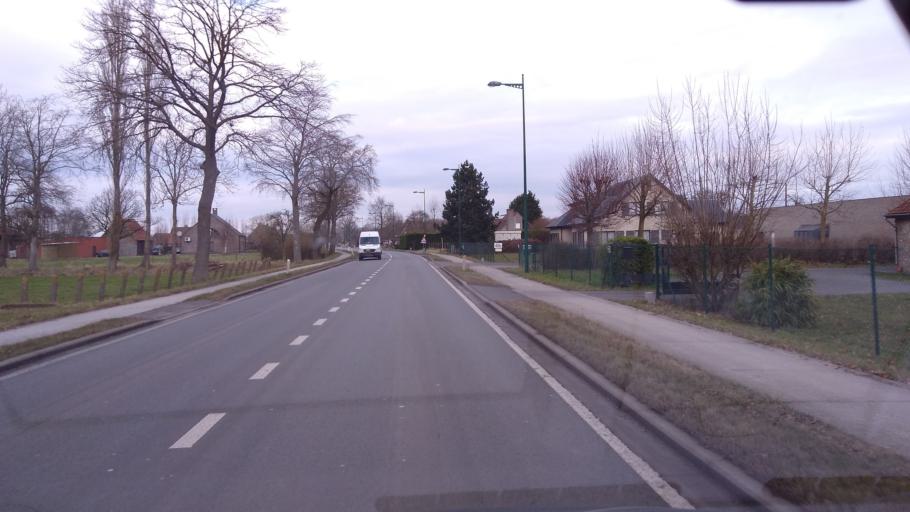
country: BE
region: Flanders
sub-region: Provincie Oost-Vlaanderen
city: Aalter
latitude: 51.0624
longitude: 3.4572
